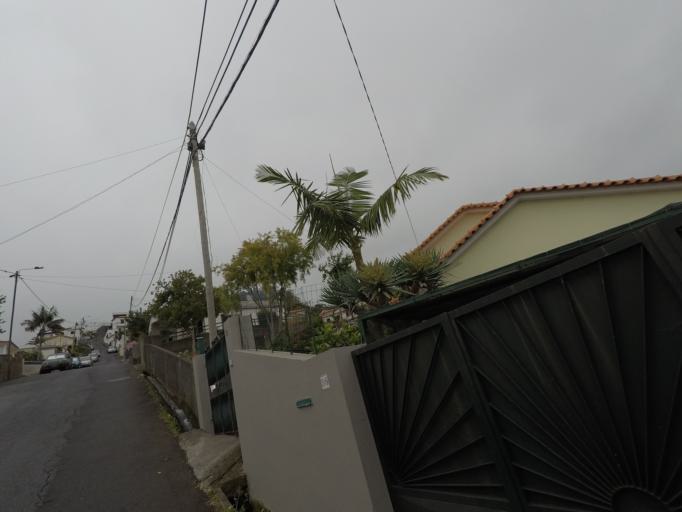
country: PT
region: Madeira
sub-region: Funchal
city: Nossa Senhora do Monte
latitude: 32.6783
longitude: -16.9430
